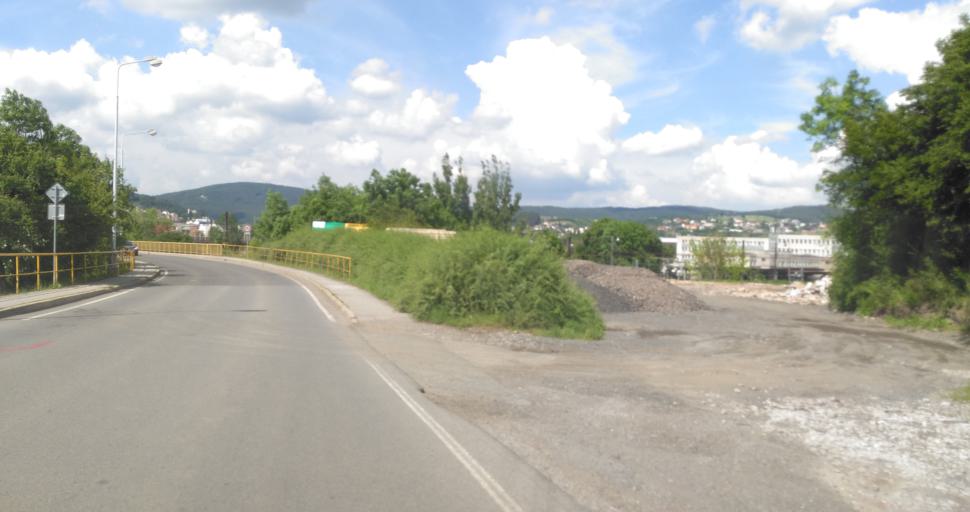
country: CZ
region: Central Bohemia
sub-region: Okres Beroun
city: Beroun
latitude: 49.9554
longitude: 14.0738
